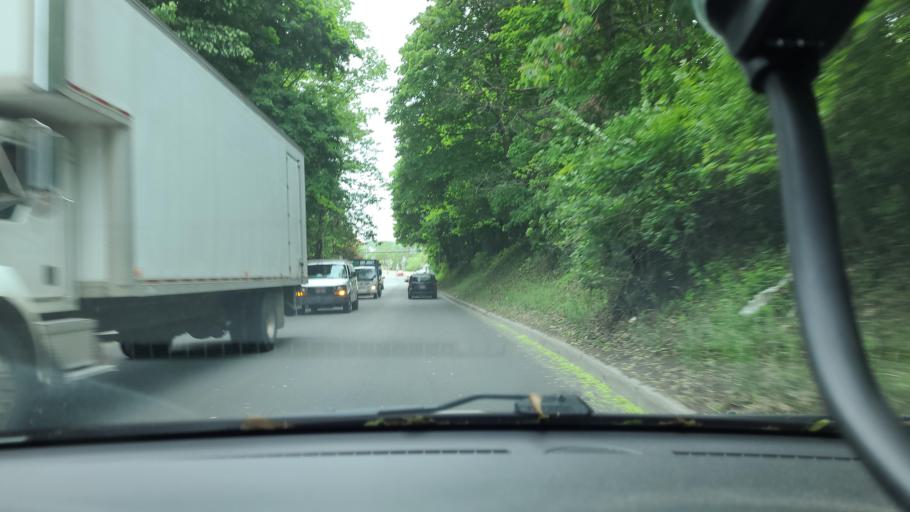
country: CA
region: Quebec
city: Montreal-Ouest
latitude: 45.4502
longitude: -73.6424
